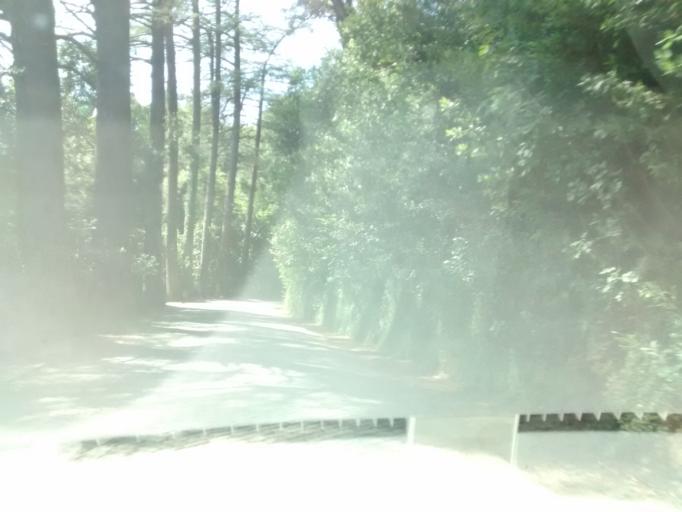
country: PT
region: Aveiro
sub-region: Mealhada
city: Pampilhosa do Botao
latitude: 40.3787
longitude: -8.3689
